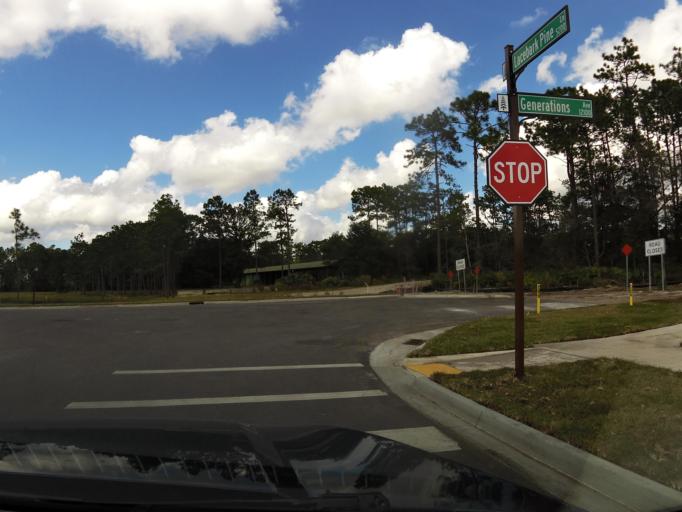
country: US
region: Florida
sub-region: Saint Johns County
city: Ponte Vedra Beach
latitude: 30.2473
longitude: -81.4952
